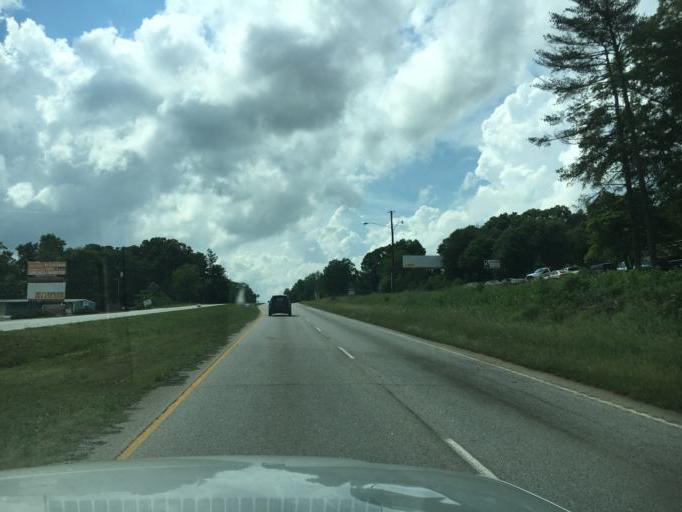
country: US
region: South Carolina
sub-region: Spartanburg County
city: Wellford
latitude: 34.9479
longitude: -82.0980
